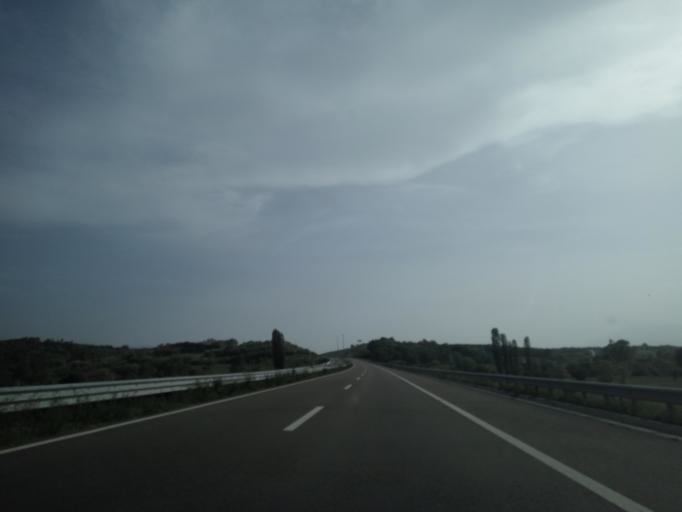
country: XK
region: Prizren
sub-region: Komuna e Therandes
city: Leshan
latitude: 42.3338
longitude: 20.7751
